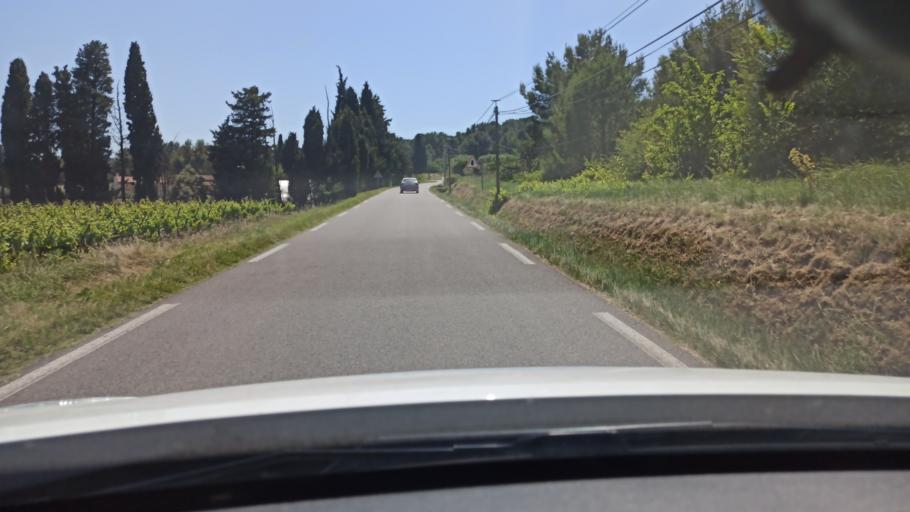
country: FR
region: Provence-Alpes-Cote d'Azur
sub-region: Departement des Bouches-du-Rhone
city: Noves
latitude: 43.8735
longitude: 4.8881
